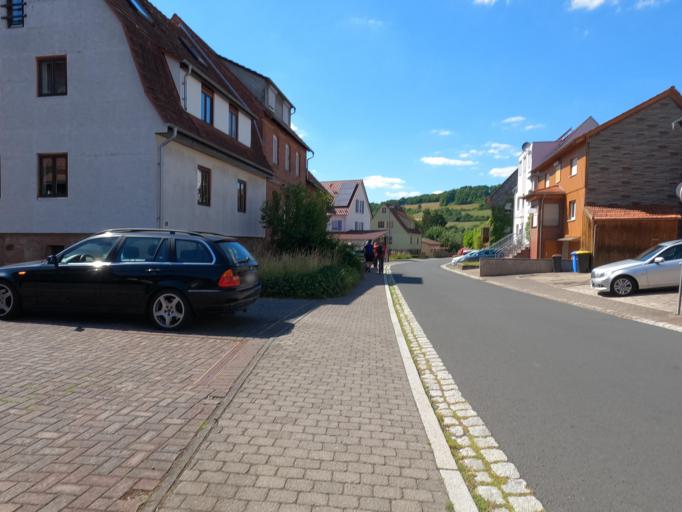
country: DE
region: Hesse
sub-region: Regierungsbezirk Darmstadt
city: Schluchtern
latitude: 50.3578
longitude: 9.5583
